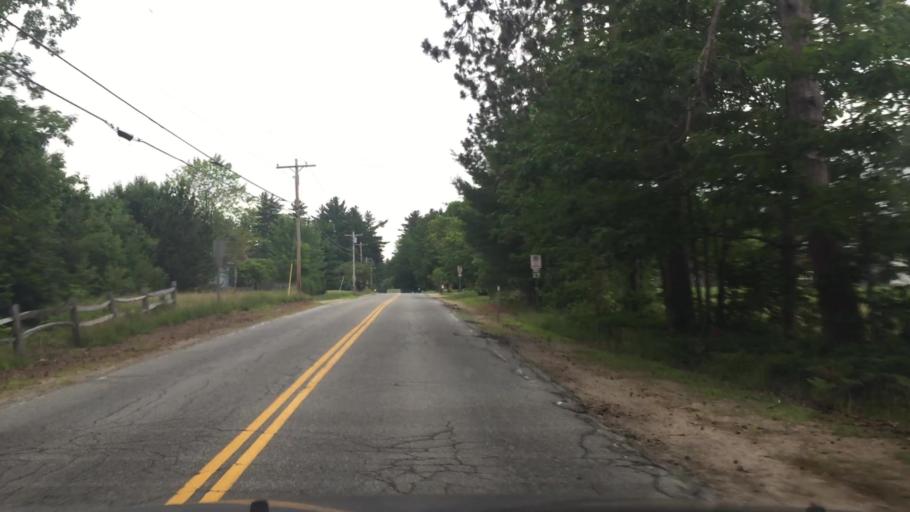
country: US
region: New Hampshire
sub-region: Carroll County
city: North Conway
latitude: 44.0725
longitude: -71.1618
